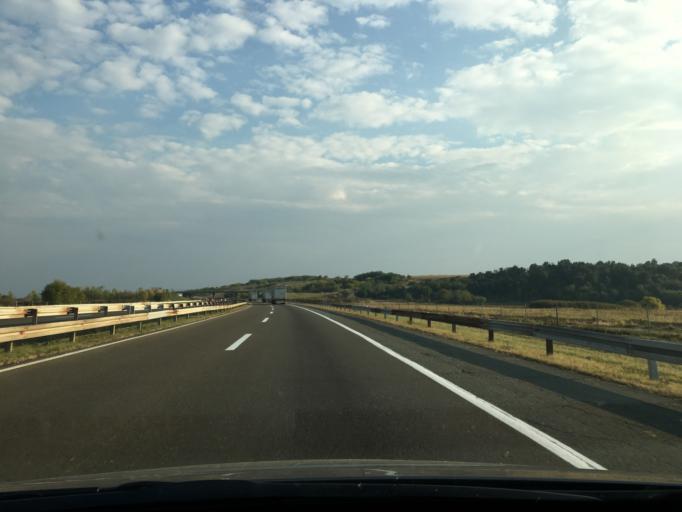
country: RS
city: Lugavcina
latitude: 44.5328
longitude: 21.0017
